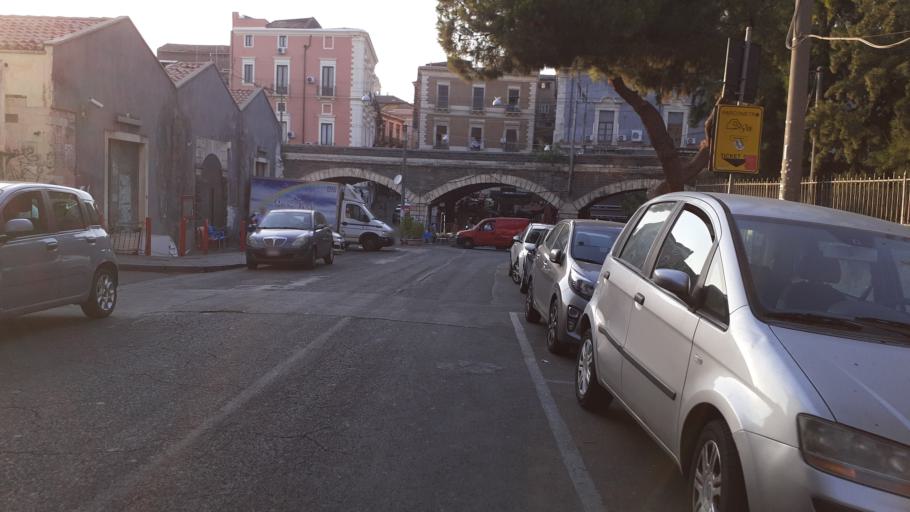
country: IT
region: Sicily
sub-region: Catania
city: Catania
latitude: 37.5008
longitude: 15.0875
